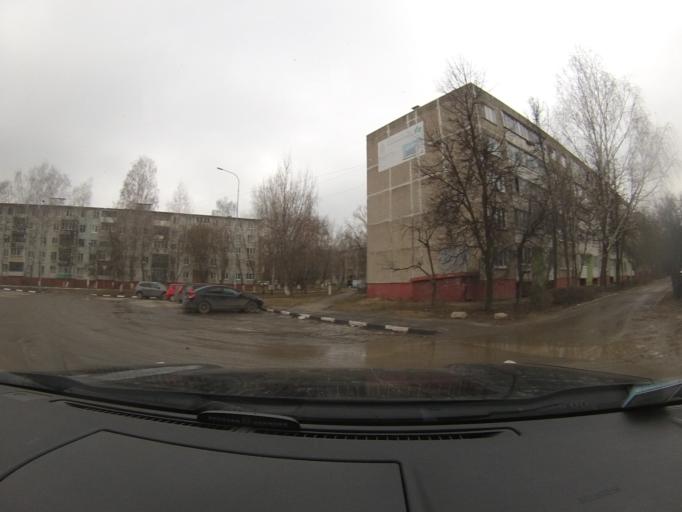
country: RU
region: Moskovskaya
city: Peski
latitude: 55.2723
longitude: 38.7488
